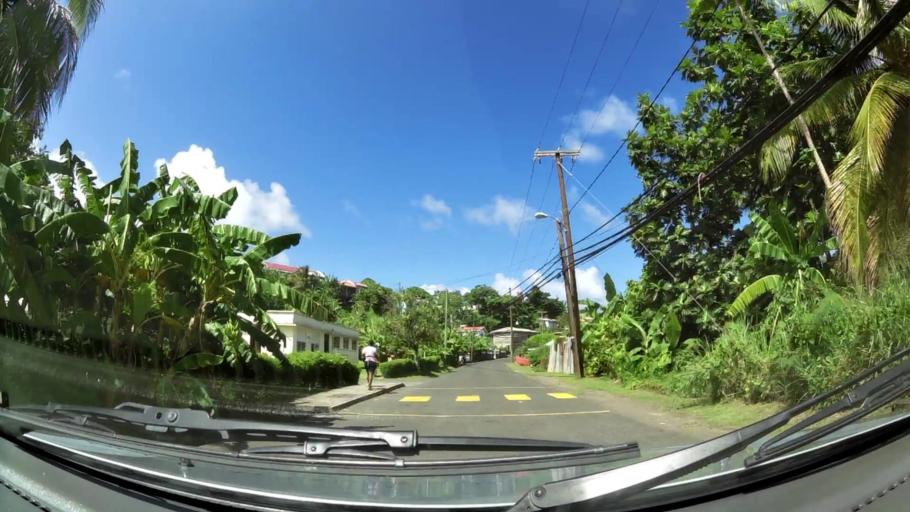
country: GD
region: Saint Patrick
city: Sauteurs
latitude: 12.2228
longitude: -61.6367
